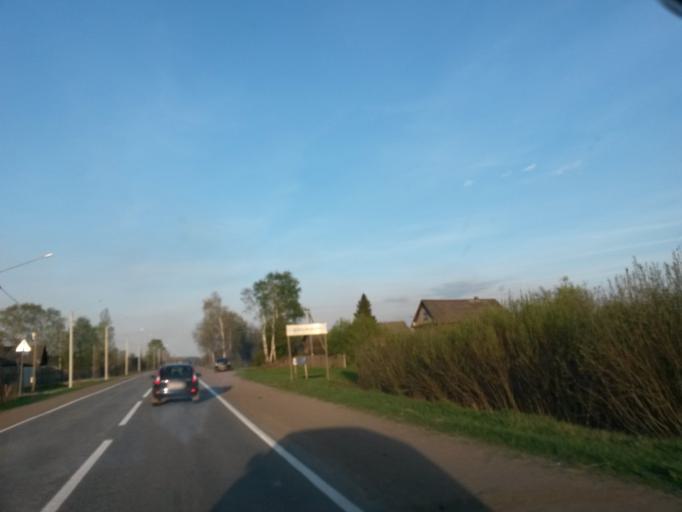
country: RU
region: Jaroslavl
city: Kurba
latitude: 57.6790
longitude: 39.5700
